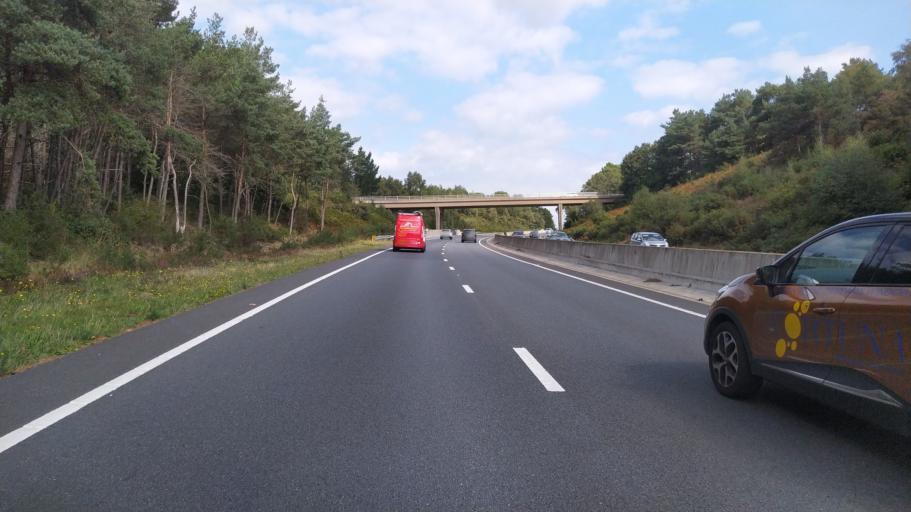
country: GB
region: England
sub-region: Hampshire
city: Ringwood
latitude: 50.8172
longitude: -1.8140
